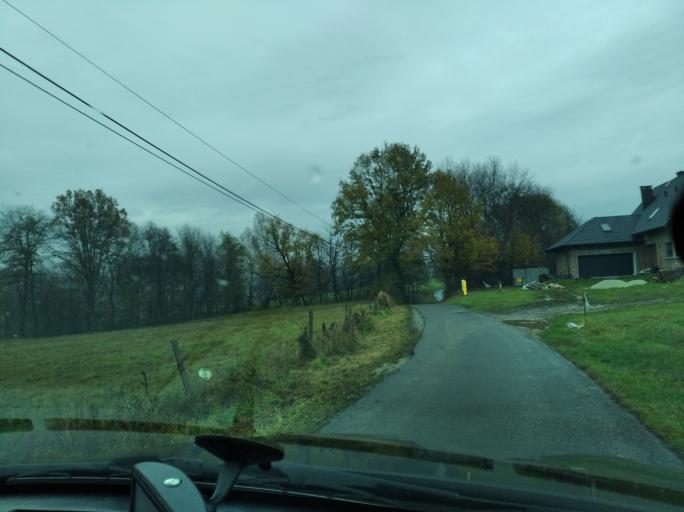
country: PL
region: Subcarpathian Voivodeship
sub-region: Powiat strzyzowski
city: Babica
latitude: 49.9302
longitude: 21.8805
